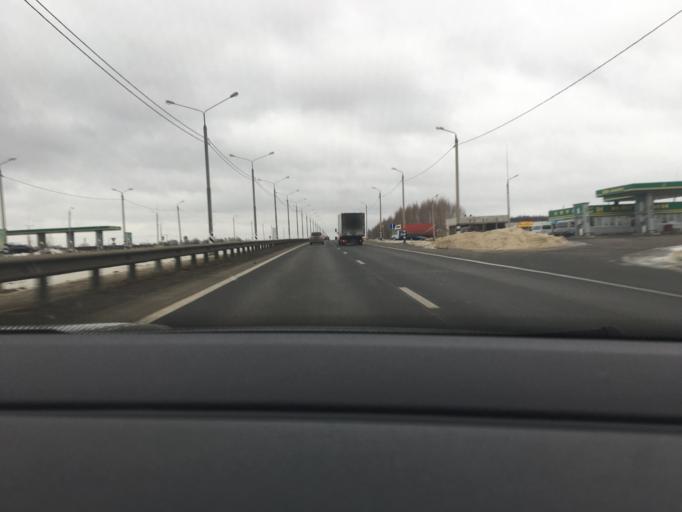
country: RU
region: Tula
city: Zaokskiy
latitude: 54.8058
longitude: 37.4838
